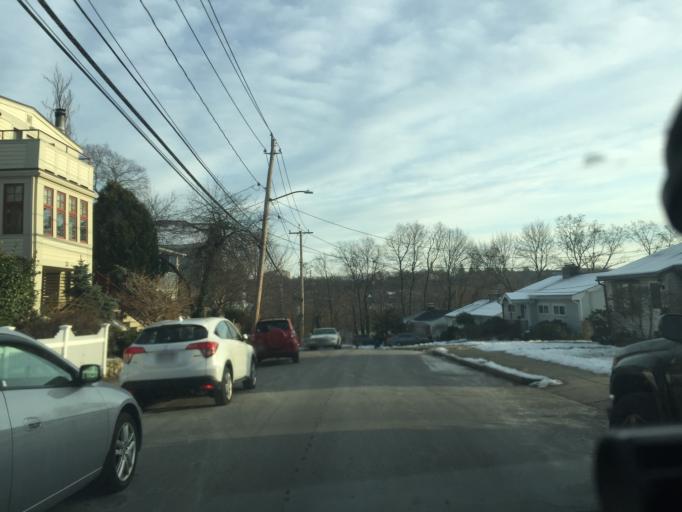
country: US
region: Massachusetts
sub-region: Middlesex County
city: Watertown
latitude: 42.3477
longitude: -71.1690
